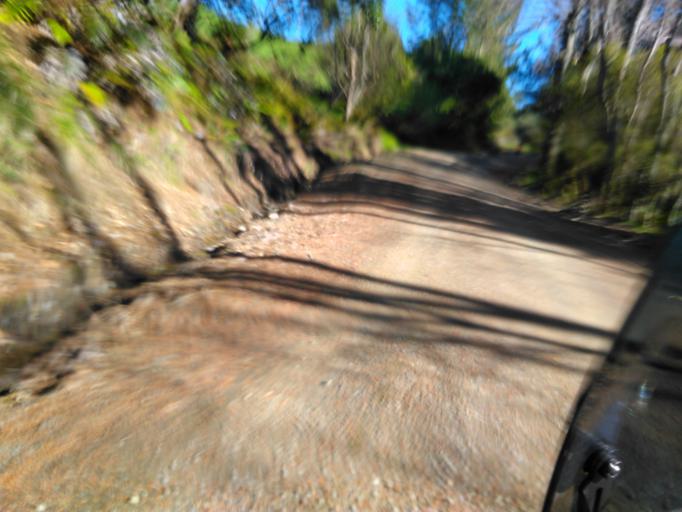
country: NZ
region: Bay of Plenty
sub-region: Opotiki District
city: Opotiki
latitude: -38.3696
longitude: 177.6005
